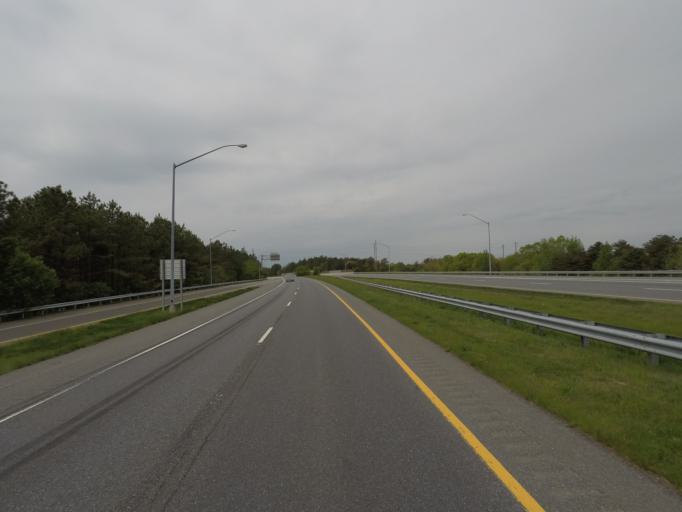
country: US
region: Maryland
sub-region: Anne Arundel County
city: Odenton
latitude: 39.1013
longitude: -76.6988
